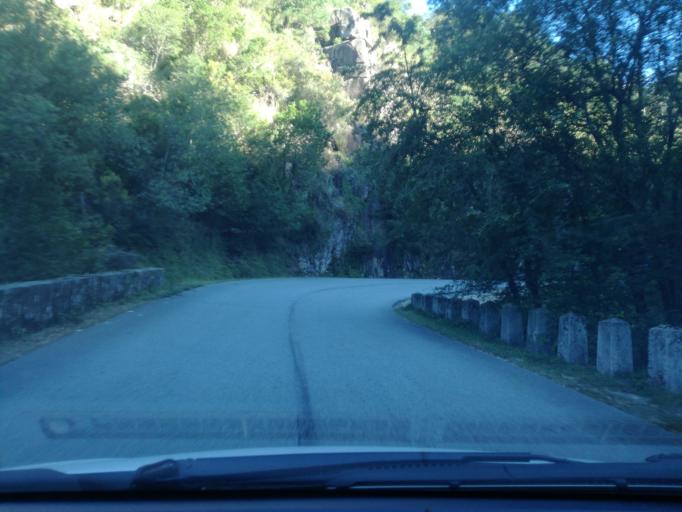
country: PT
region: Braga
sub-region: Vieira do Minho
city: Real
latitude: 41.7609
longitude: -8.1490
